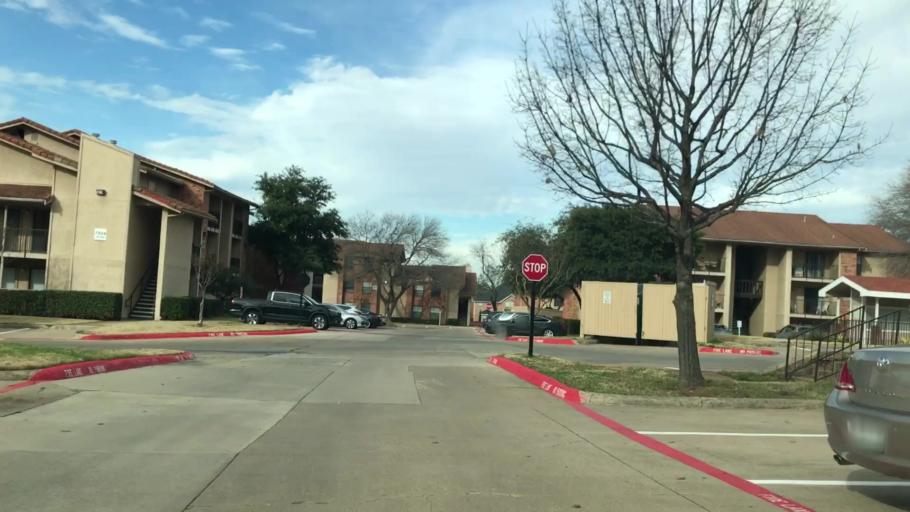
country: US
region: Texas
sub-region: Dallas County
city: Farmers Branch
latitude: 32.9054
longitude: -96.9618
